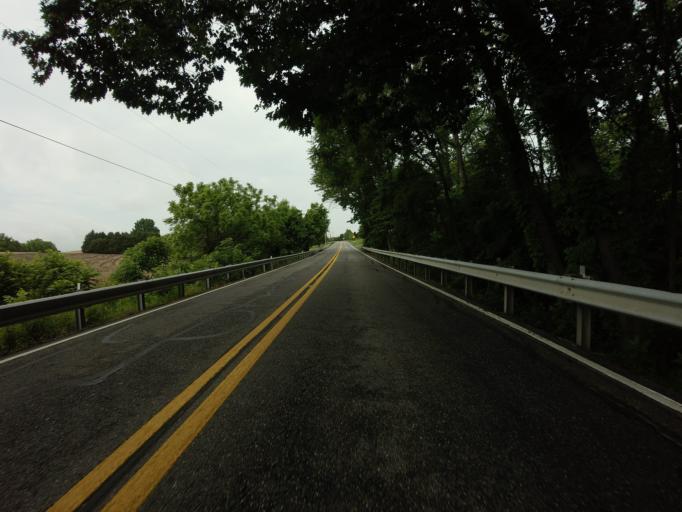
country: US
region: Maryland
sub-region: Frederick County
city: Brunswick
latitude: 39.3228
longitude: -77.5996
